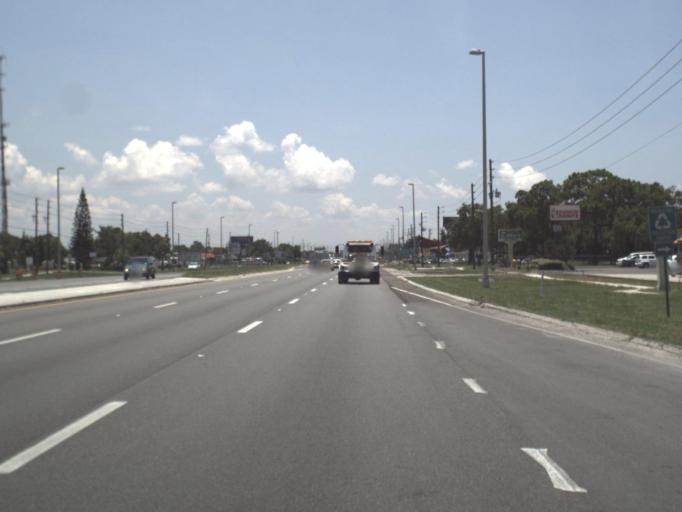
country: US
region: Florida
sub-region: Pasco County
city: Bayonet Point
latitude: 28.3239
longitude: -82.6994
